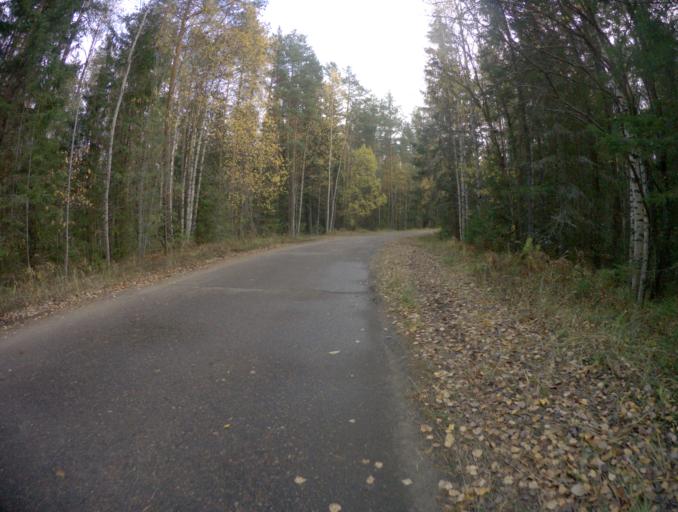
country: RU
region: Vladimir
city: Raduzhnyy
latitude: 55.9322
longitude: 40.3511
